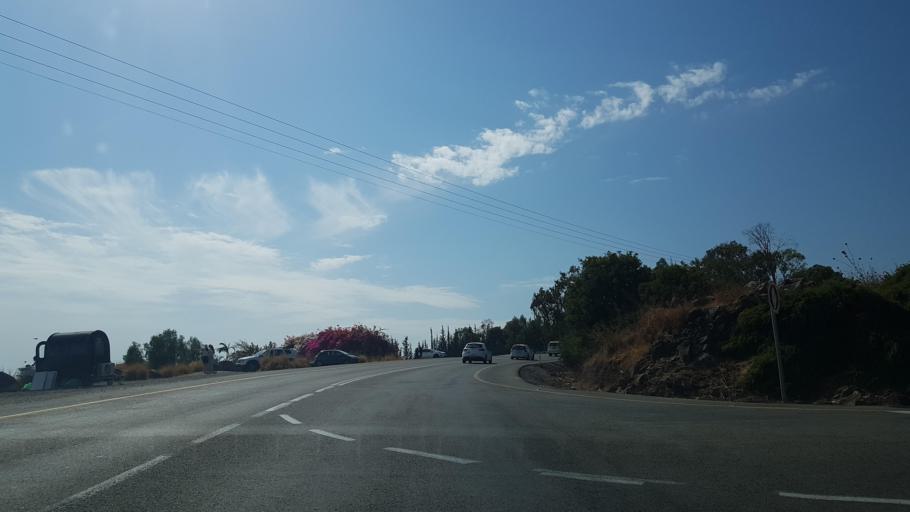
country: IL
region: Northern District
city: Rosh Pinna
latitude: 32.9039
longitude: 35.5536
